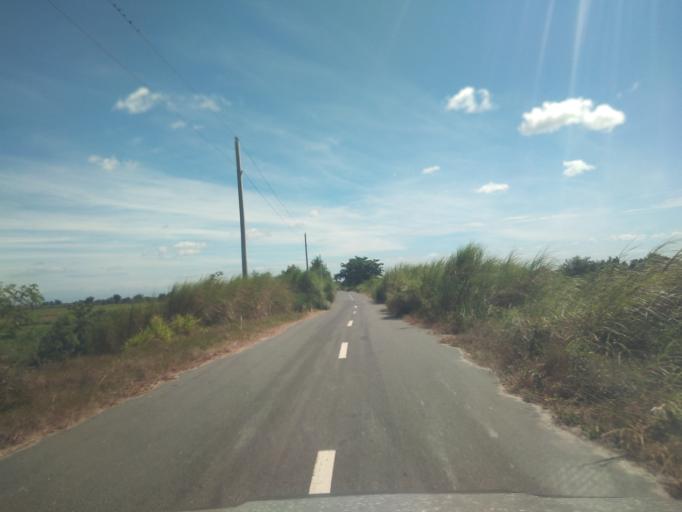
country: PH
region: Central Luzon
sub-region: Province of Pampanga
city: Balas
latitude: 15.0527
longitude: 120.5787
